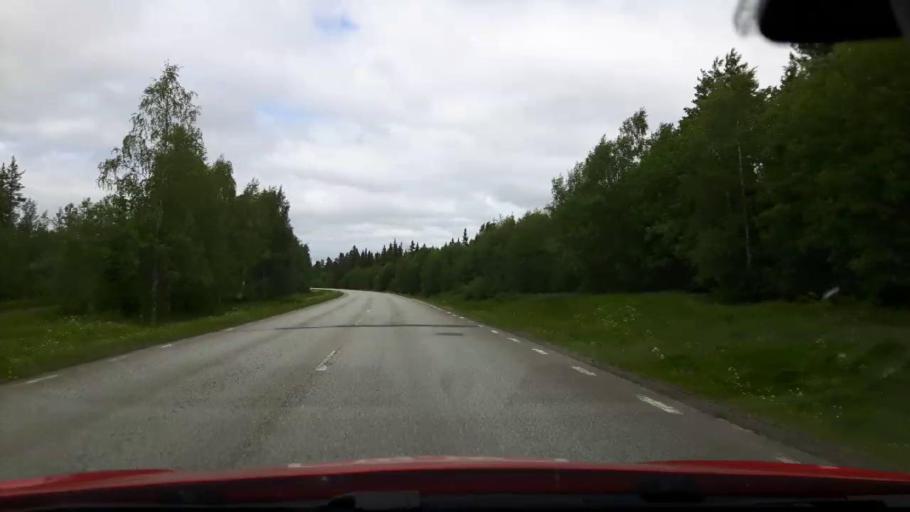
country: SE
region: Jaemtland
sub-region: Krokoms Kommun
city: Krokom
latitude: 63.4301
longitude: 14.4987
